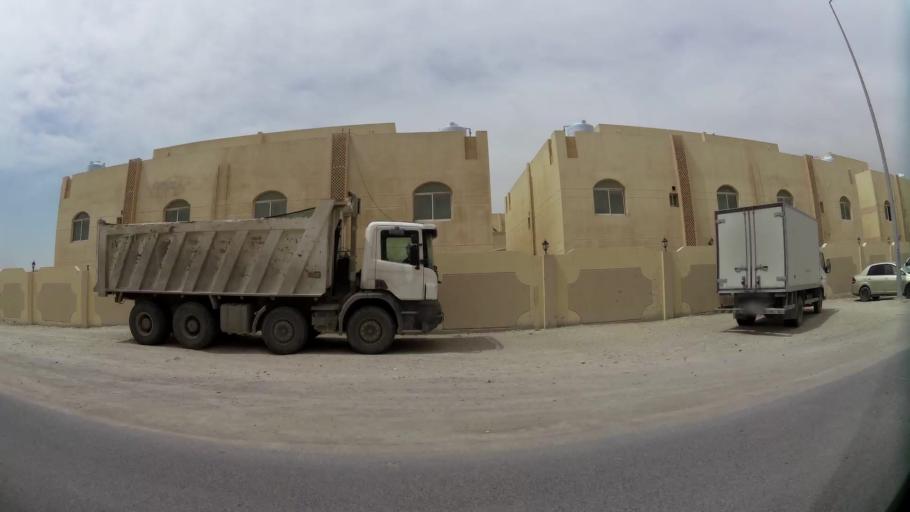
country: QA
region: Baladiyat ar Rayyan
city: Ar Rayyan
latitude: 25.2215
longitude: 51.4616
